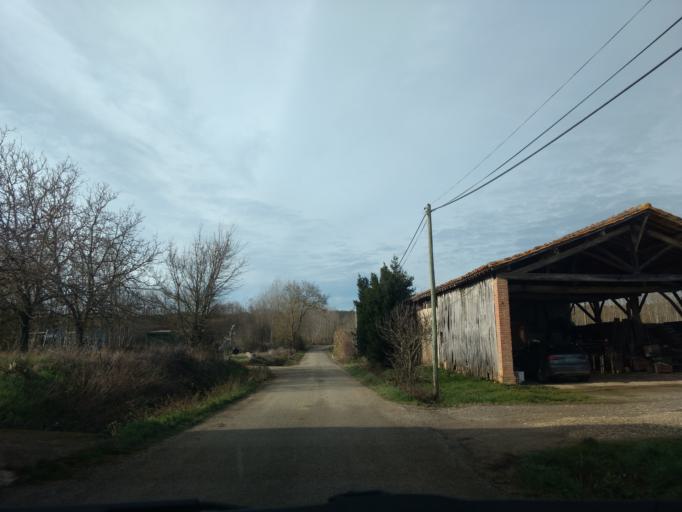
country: FR
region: Midi-Pyrenees
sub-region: Departement du Gers
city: Aubiet
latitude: 43.6719
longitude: 0.8024
